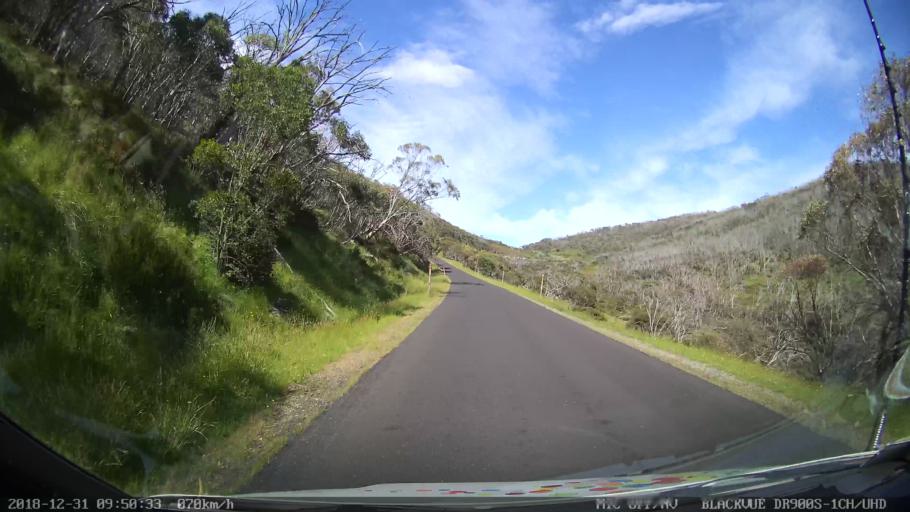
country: AU
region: New South Wales
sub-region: Snowy River
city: Jindabyne
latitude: -36.5207
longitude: 148.2718
